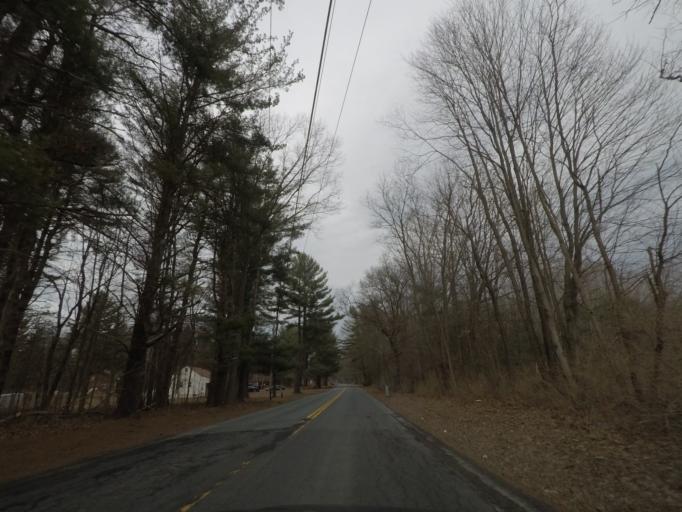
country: US
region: New York
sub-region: Saratoga County
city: Stillwater
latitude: 42.9239
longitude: -73.5134
